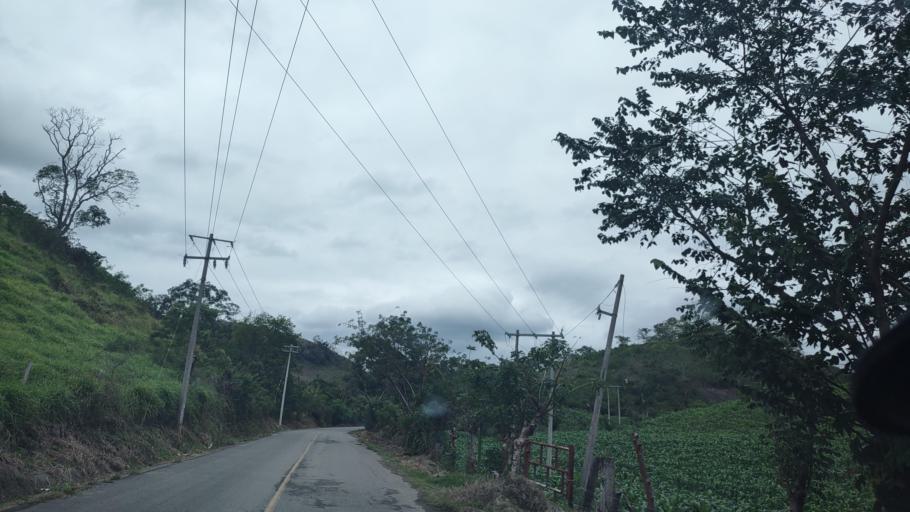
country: MX
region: Veracruz
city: Papantla de Olarte
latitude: 20.4446
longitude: -97.2923
